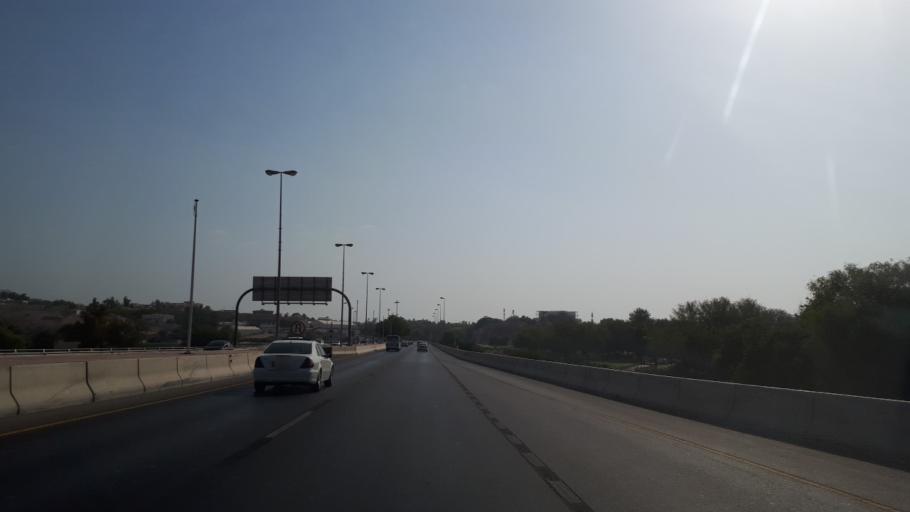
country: OM
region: Muhafazat Masqat
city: Muscat
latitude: 23.6160
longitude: 58.4906
